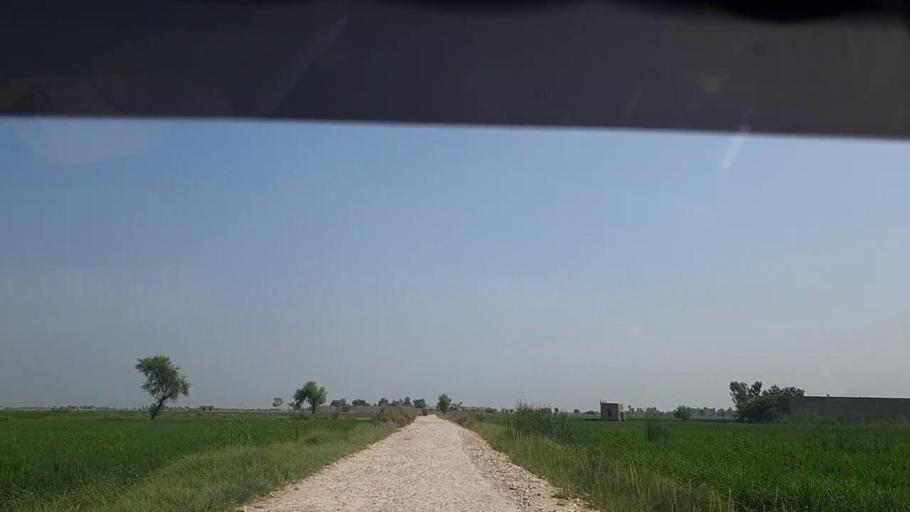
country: PK
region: Sindh
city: Thul
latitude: 28.1974
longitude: 68.7319
